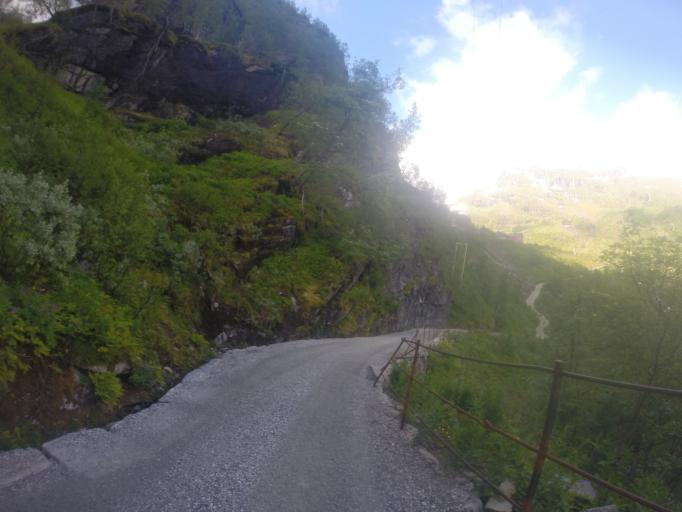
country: NO
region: Sogn og Fjordane
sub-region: Aurland
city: Aurlandsvangen
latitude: 60.7413
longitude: 7.1270
